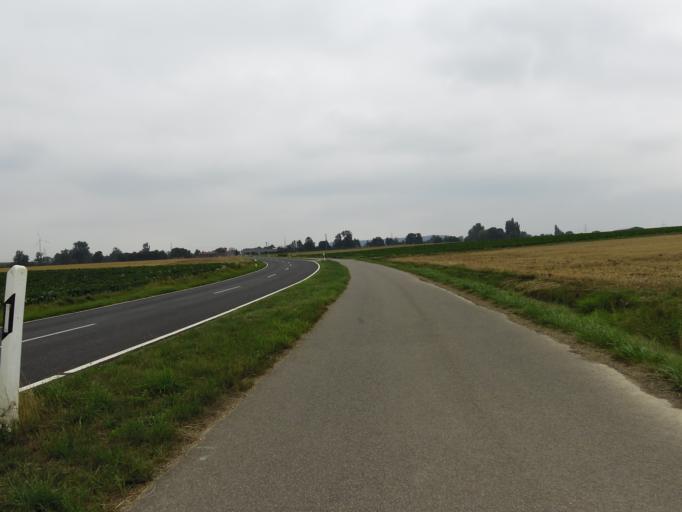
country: DE
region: North Rhine-Westphalia
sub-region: Regierungsbezirk Koln
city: Linnich
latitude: 50.9549
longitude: 6.2526
